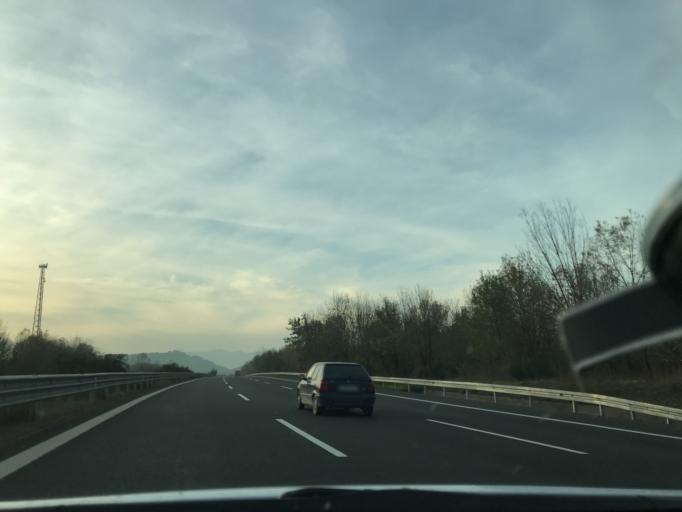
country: TR
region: Duzce
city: Gumusova
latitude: 40.8395
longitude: 30.9858
